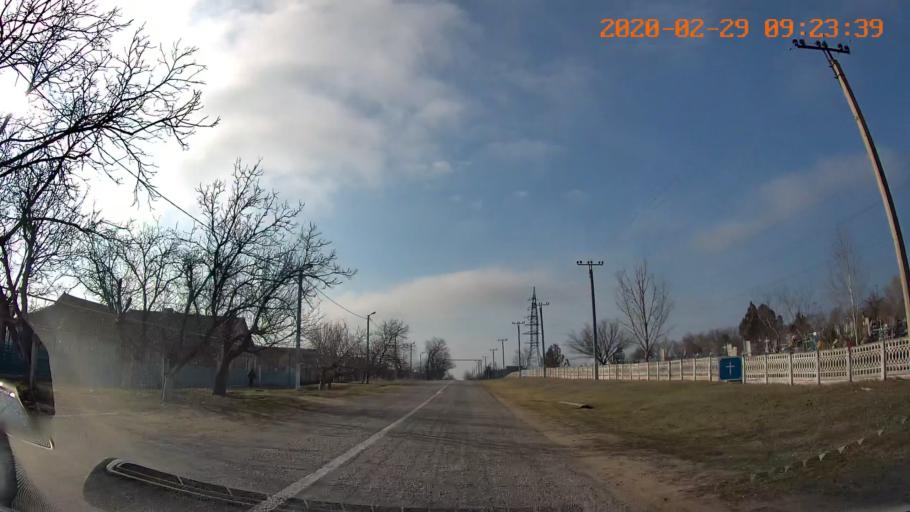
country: MD
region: Telenesti
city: Pervomaisc
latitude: 46.7237
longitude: 29.9607
